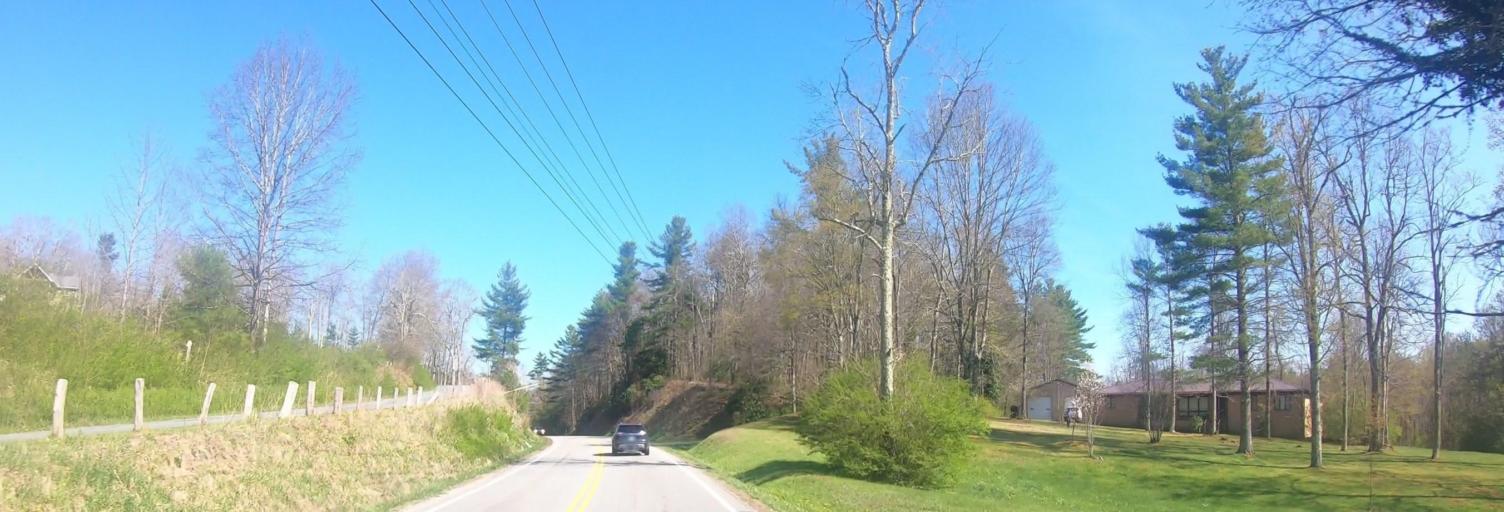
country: US
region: North Carolina
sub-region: Avery County
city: Newland
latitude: 36.0316
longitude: -81.9036
